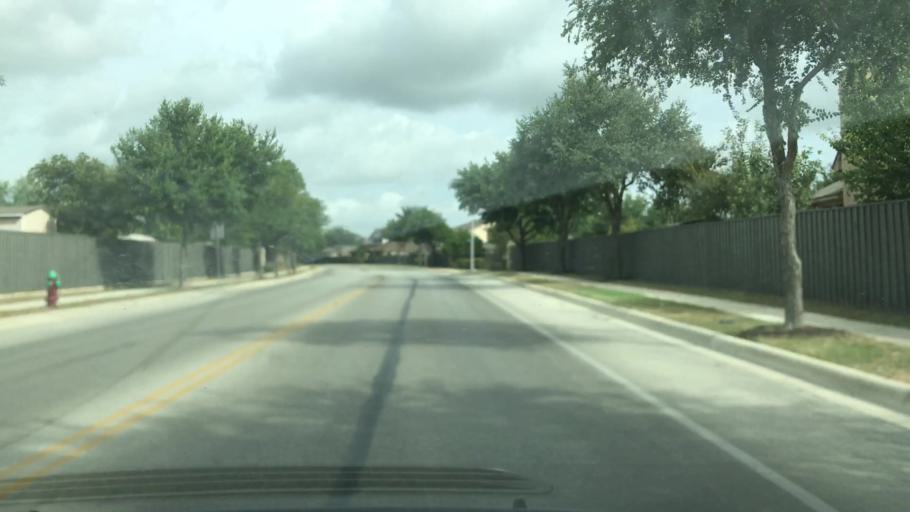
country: US
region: Texas
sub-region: Guadalupe County
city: Cibolo
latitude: 29.5819
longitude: -98.2406
